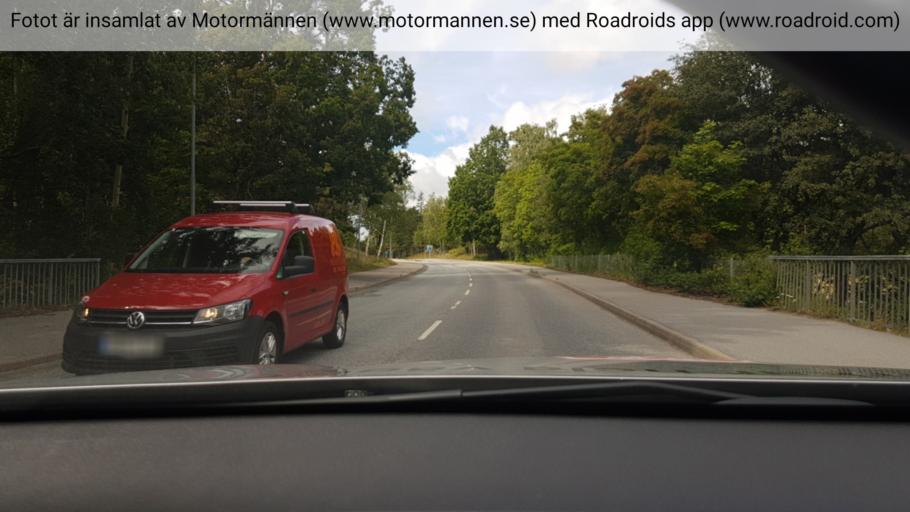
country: SE
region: Stockholm
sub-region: Tyreso Kommun
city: Bollmora
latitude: 59.2352
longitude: 18.2236
